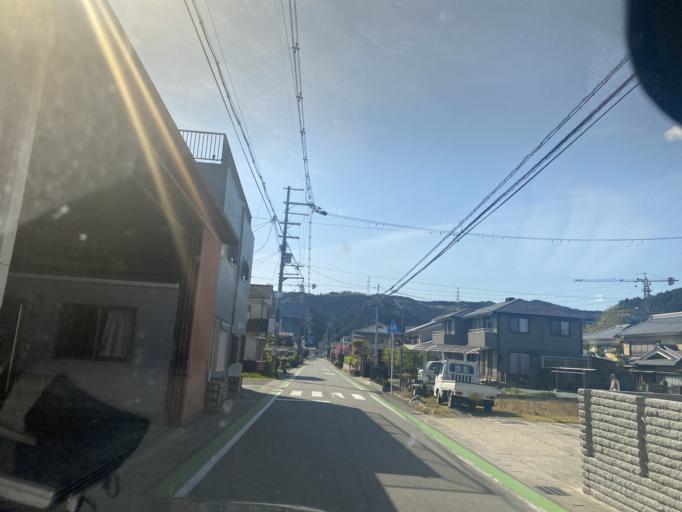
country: JP
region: Kyoto
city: Uji
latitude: 34.8526
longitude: 135.8509
